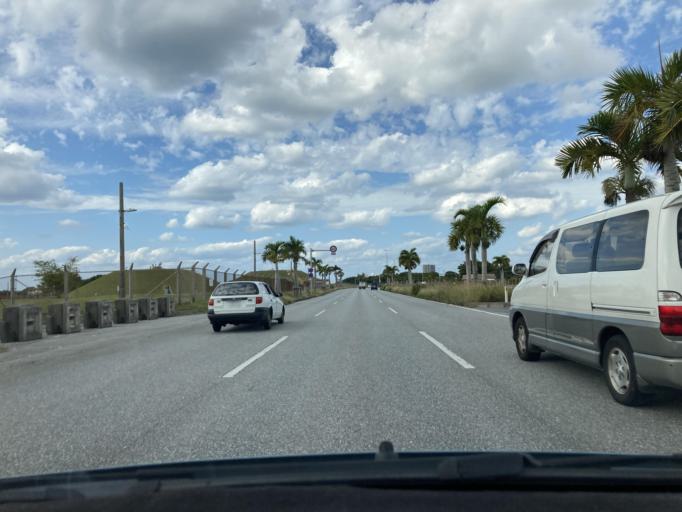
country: JP
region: Okinawa
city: Chatan
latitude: 26.3442
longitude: 127.7481
